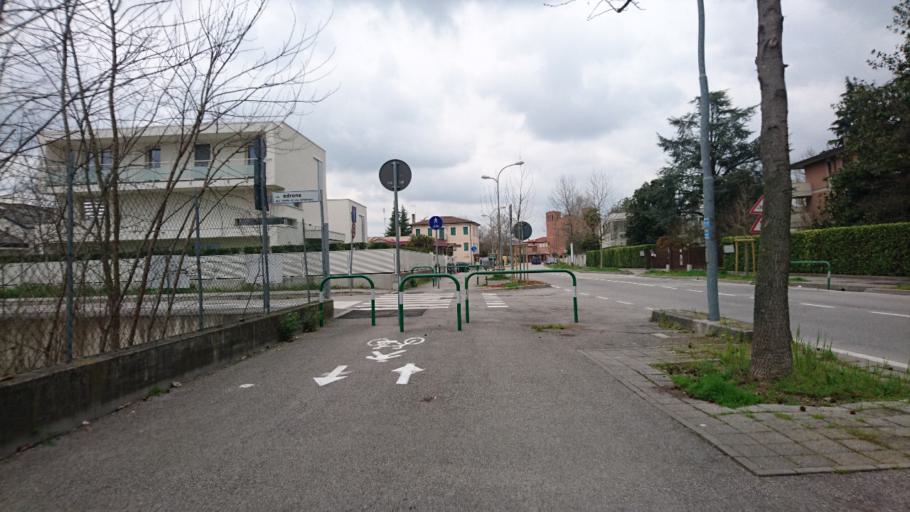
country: IT
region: Veneto
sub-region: Provincia di Padova
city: Vigodarzere
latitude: 45.4453
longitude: 11.8715
